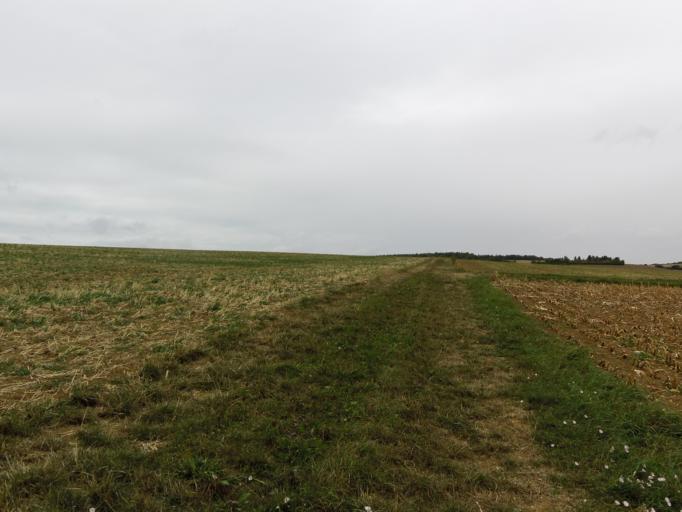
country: DE
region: Bavaria
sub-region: Regierungsbezirk Unterfranken
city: Rimpar
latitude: 49.8576
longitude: 9.9404
